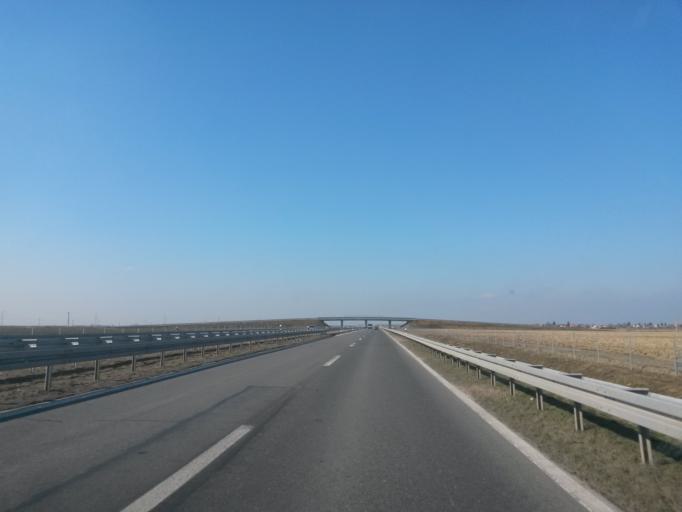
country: HR
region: Osjecko-Baranjska
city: Visnjevac
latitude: 45.5628
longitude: 18.5958
